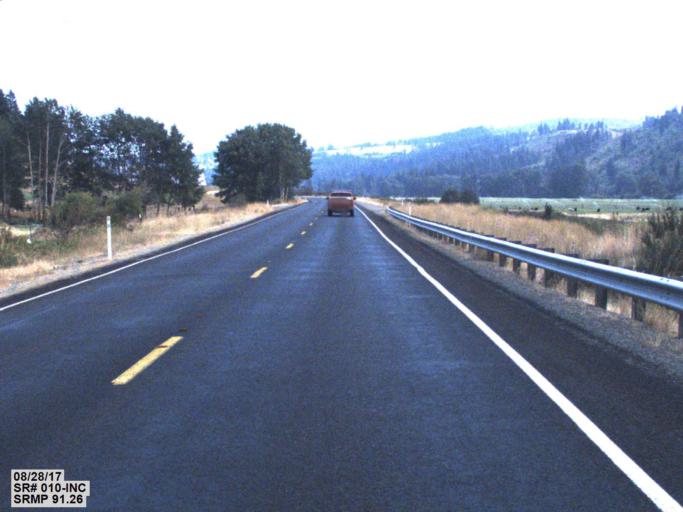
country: US
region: Washington
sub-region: Kittitas County
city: Cle Elum
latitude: 47.1541
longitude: -120.8062
